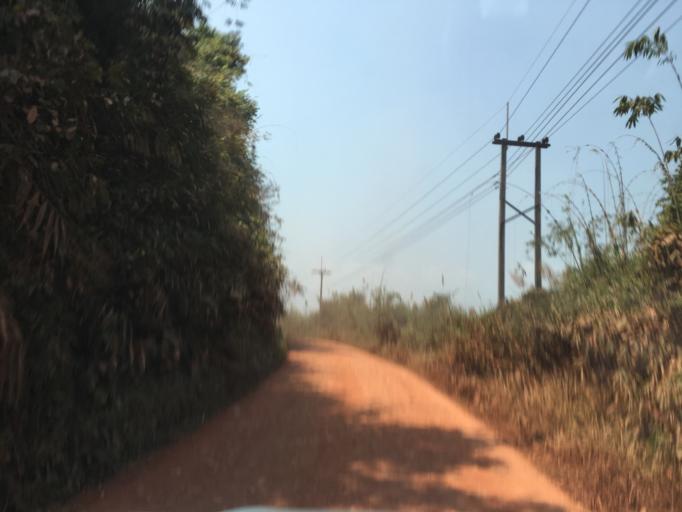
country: LA
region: Bolikhamxai
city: Bolikhan
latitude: 18.7508
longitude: 103.6094
